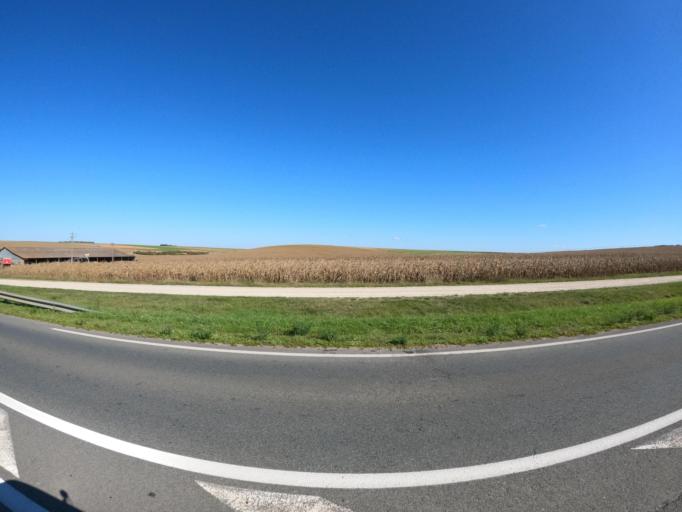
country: FR
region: Poitou-Charentes
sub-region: Departement de la Vienne
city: Cisse
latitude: 46.6417
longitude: 0.2020
